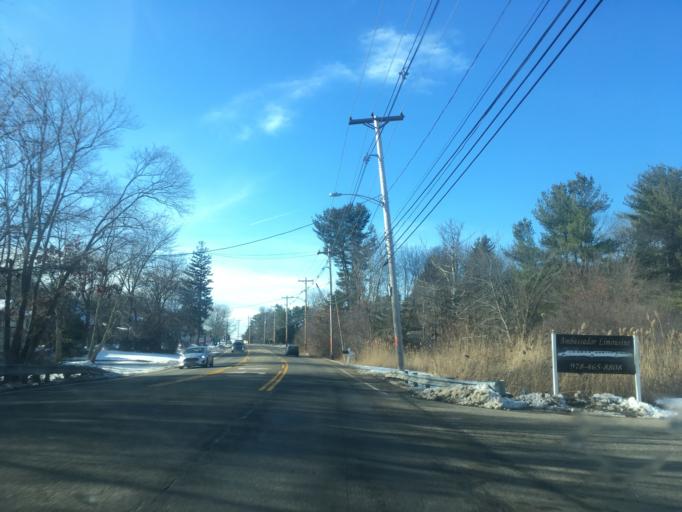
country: US
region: Massachusetts
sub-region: Essex County
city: Salisbury
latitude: 42.8445
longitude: -70.8823
